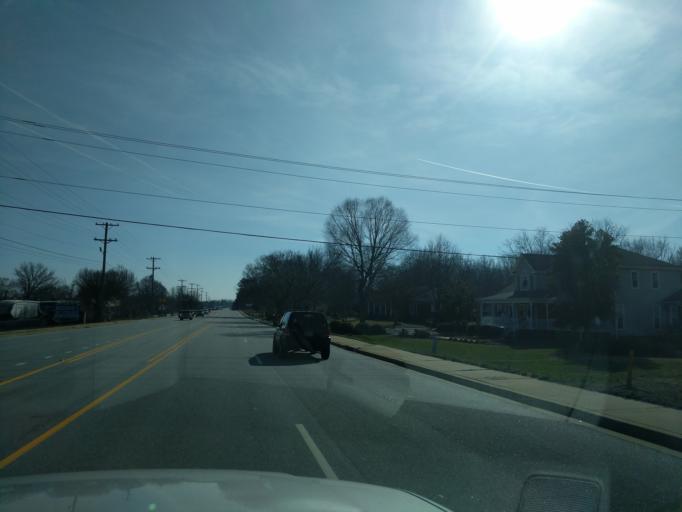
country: US
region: South Carolina
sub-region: Spartanburg County
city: Duncan
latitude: 34.8798
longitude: -82.1477
